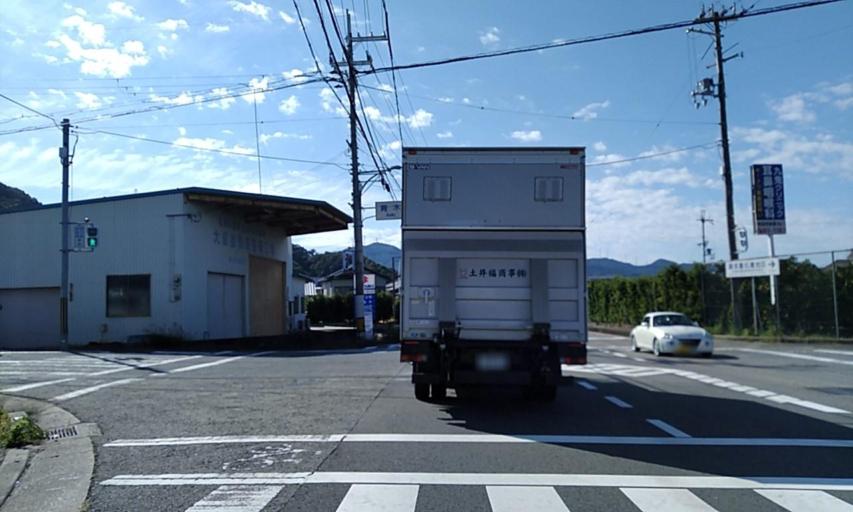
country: JP
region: Wakayama
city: Kainan
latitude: 34.0327
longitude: 135.1854
